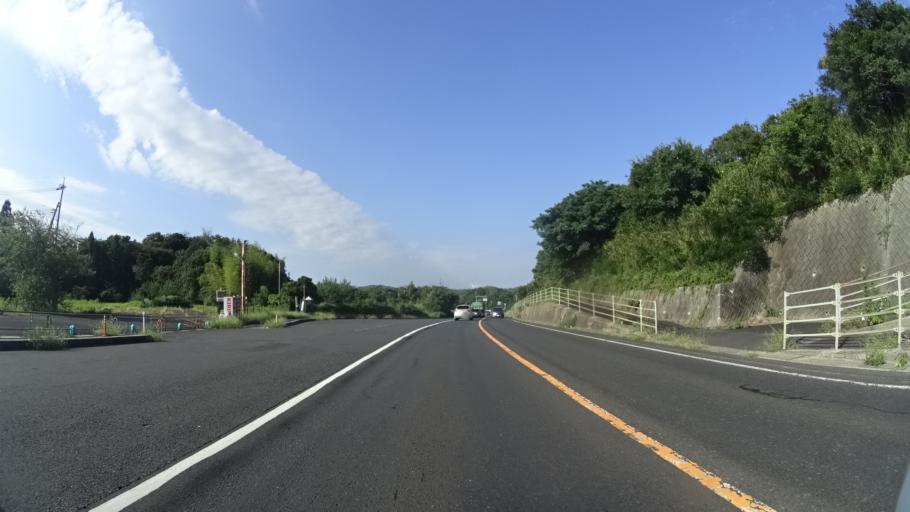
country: JP
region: Shimane
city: Izumo
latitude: 35.3035
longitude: 132.6529
